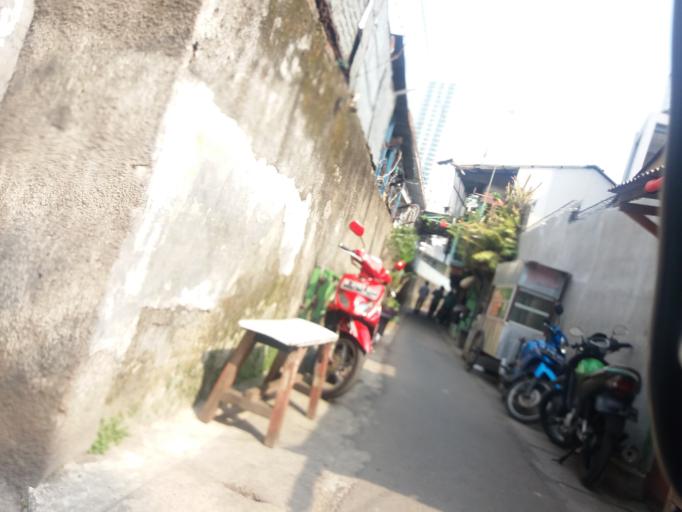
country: ID
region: Jakarta Raya
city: Jakarta
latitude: -6.2189
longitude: 106.8253
